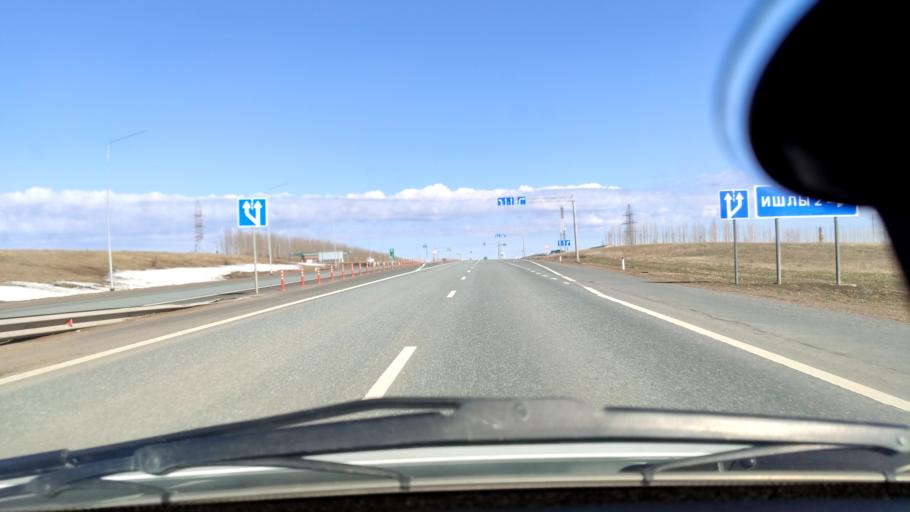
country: RU
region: Bashkortostan
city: Tolbazy
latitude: 54.1944
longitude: 55.8903
